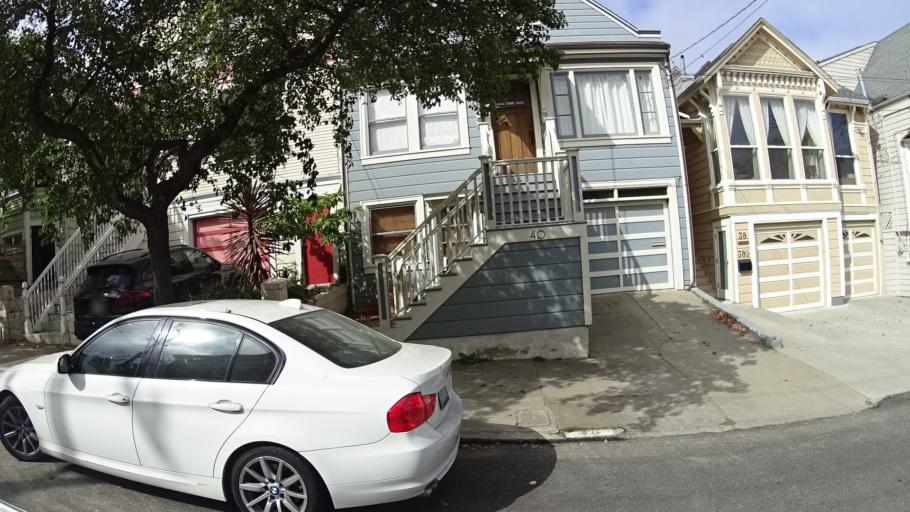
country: US
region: California
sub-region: San Francisco County
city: San Francisco
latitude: 37.7409
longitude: -122.4278
